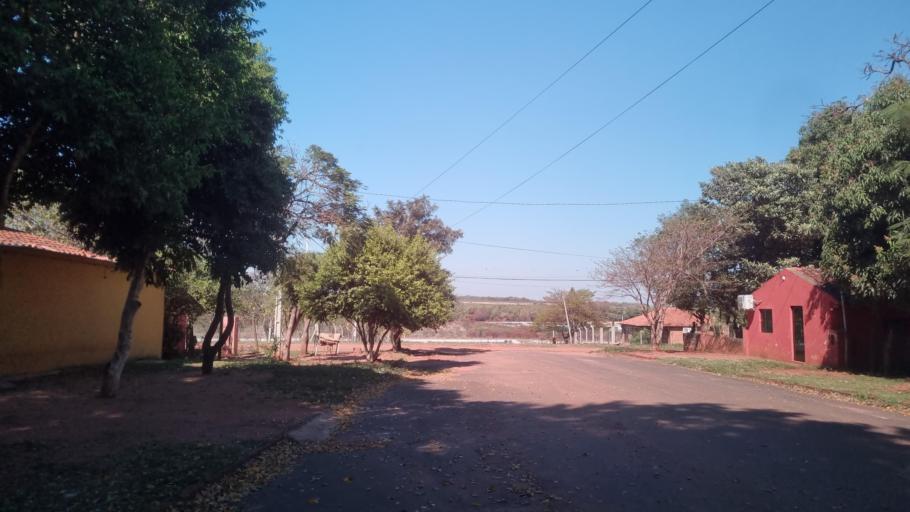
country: PY
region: Misiones
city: San Juan Bautista
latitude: -26.6778
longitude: -57.1471
